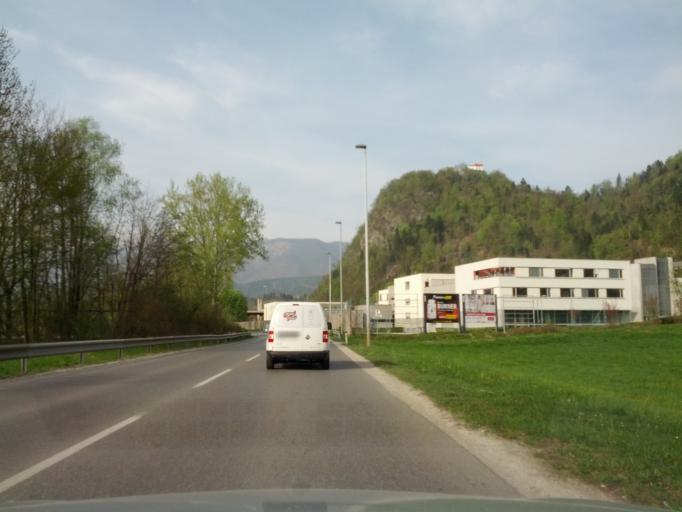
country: SI
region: Kamnik
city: Kamnik
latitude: 46.2177
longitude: 14.6095
